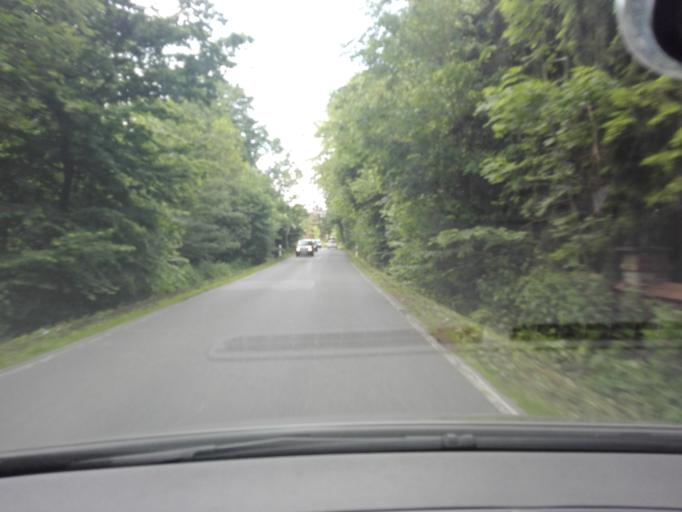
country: DE
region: North Rhine-Westphalia
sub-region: Regierungsbezirk Arnsberg
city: Frondenberg
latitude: 51.4823
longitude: 7.7602
